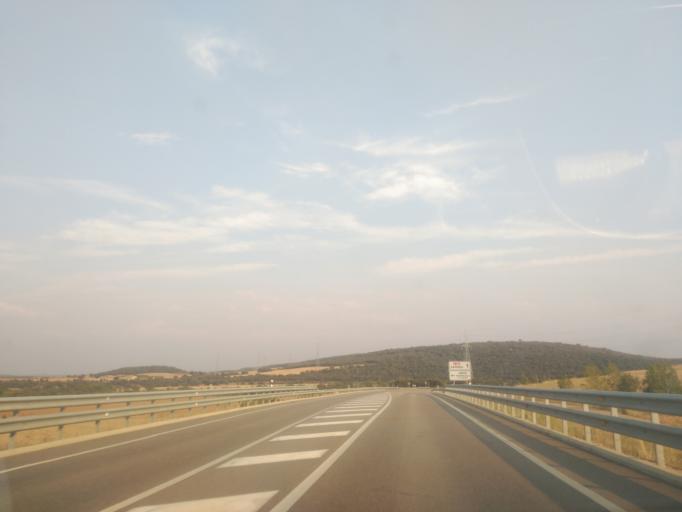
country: ES
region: Castille and Leon
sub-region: Provincia de Zamora
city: Moreruela de Tabara
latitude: 41.7598
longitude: -5.8591
